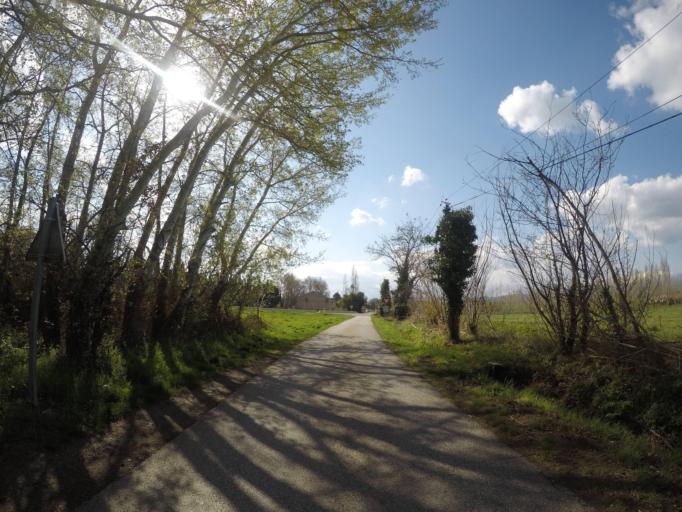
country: FR
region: Languedoc-Roussillon
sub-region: Departement des Pyrenees-Orientales
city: Millas
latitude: 42.6845
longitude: 2.6961
